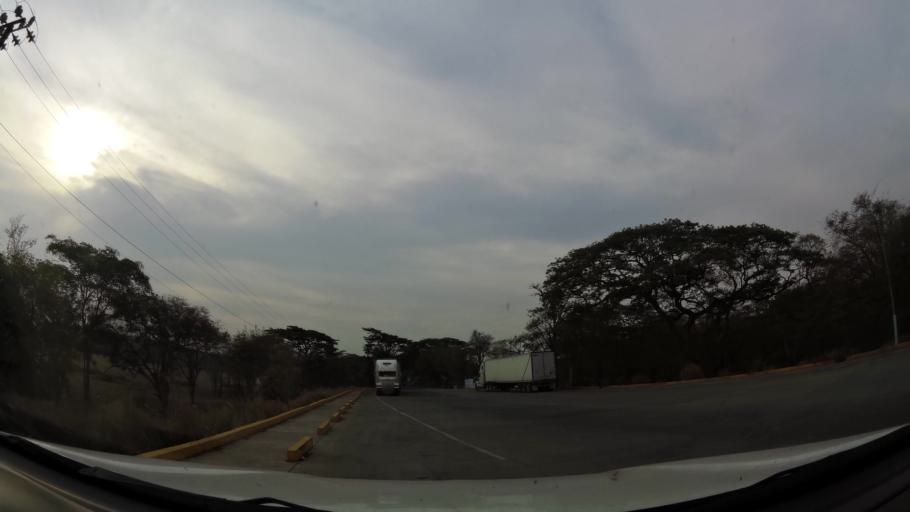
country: NI
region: Rivas
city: Cardenas
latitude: 11.2194
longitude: -85.6145
